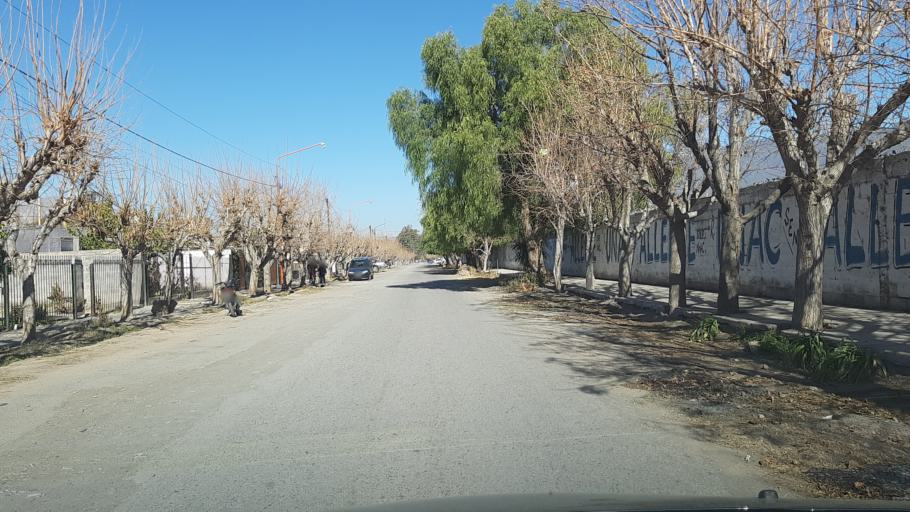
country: AR
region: San Juan
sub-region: Departamento de Zonda
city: Zonda
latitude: -31.5466
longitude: -68.7271
